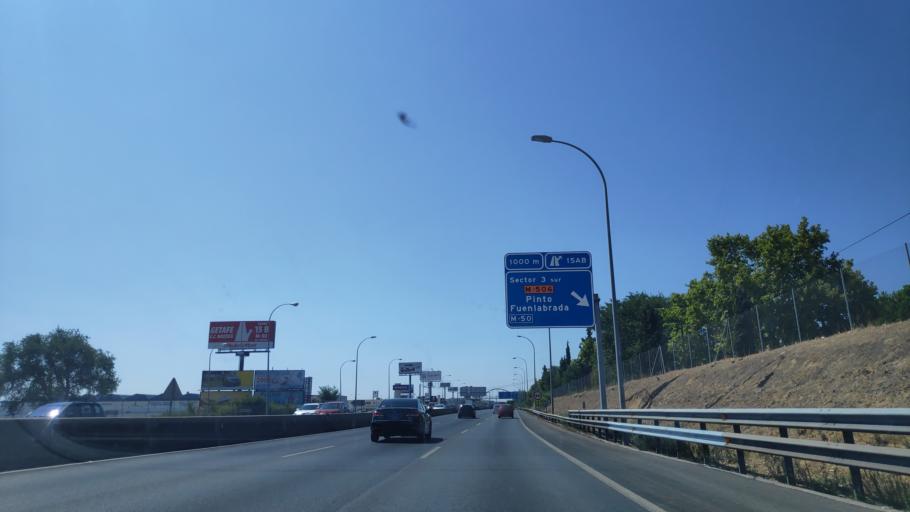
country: ES
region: Madrid
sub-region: Provincia de Madrid
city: Getafe
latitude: 40.2950
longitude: -3.7382
